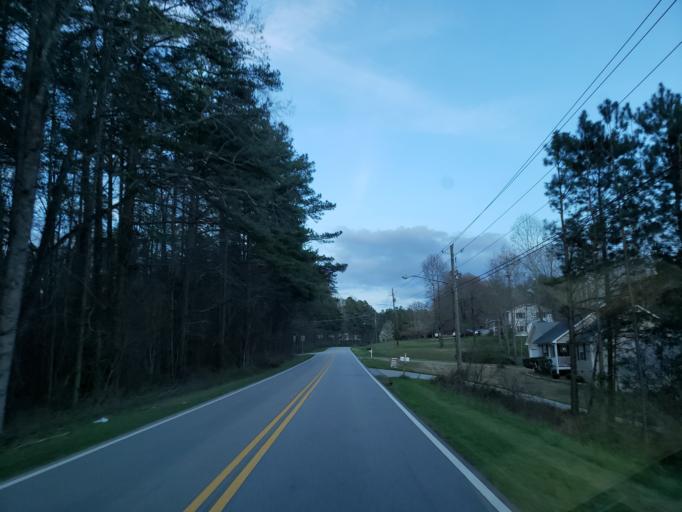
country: US
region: Georgia
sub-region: Polk County
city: Rockmart
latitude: 33.9901
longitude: -84.9604
